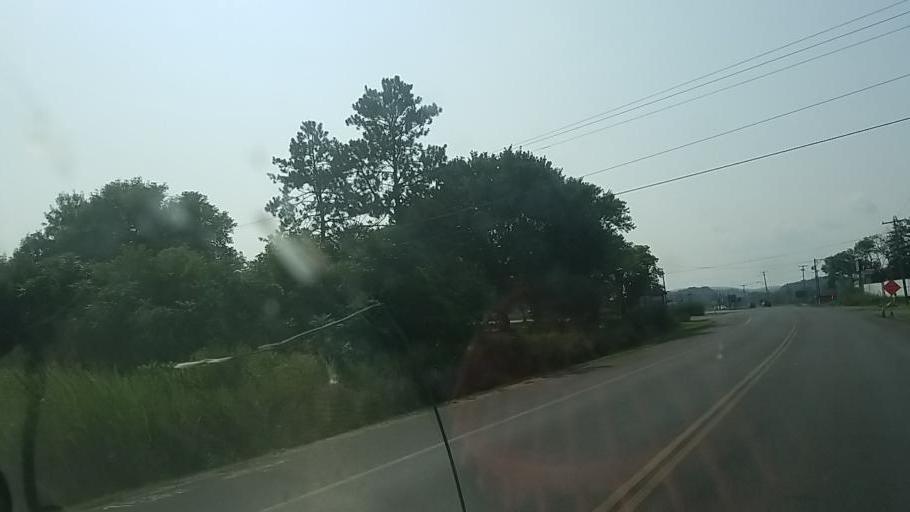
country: US
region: New York
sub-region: Montgomery County
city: Fonda
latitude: 42.9480
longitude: -74.3560
